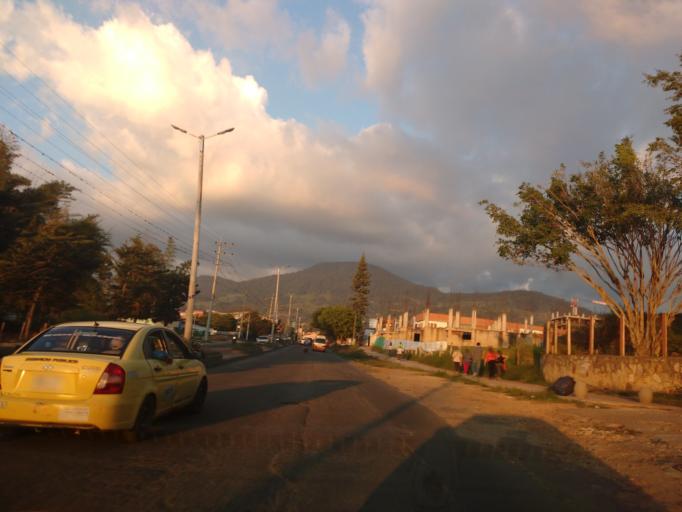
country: CO
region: Cundinamarca
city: Fusagasuga
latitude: 4.3317
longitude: -74.3752
